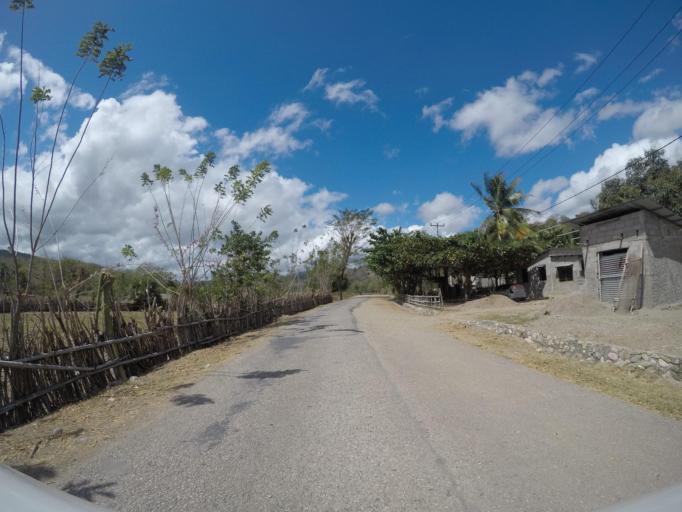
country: TL
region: Lautem
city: Lospalos
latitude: -8.4733
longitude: 126.8174
